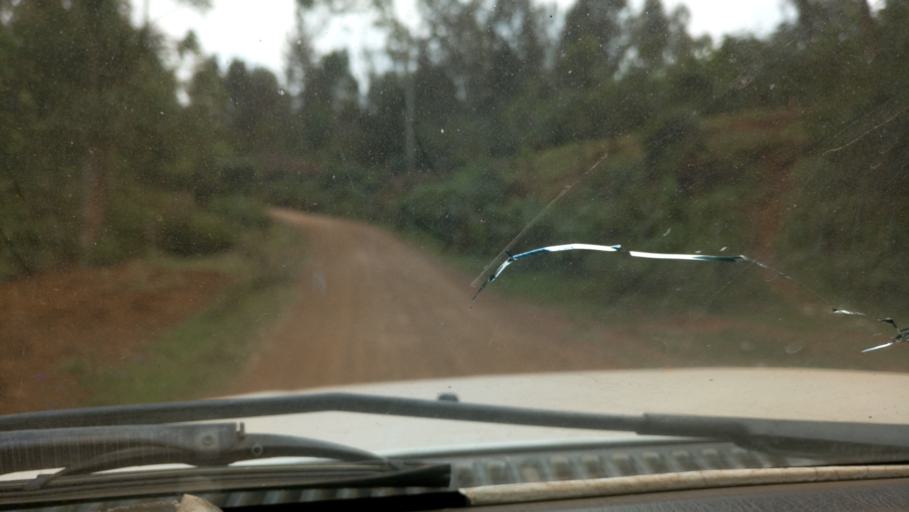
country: KE
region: Murang'a District
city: Maragua
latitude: -0.8310
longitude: 37.0054
